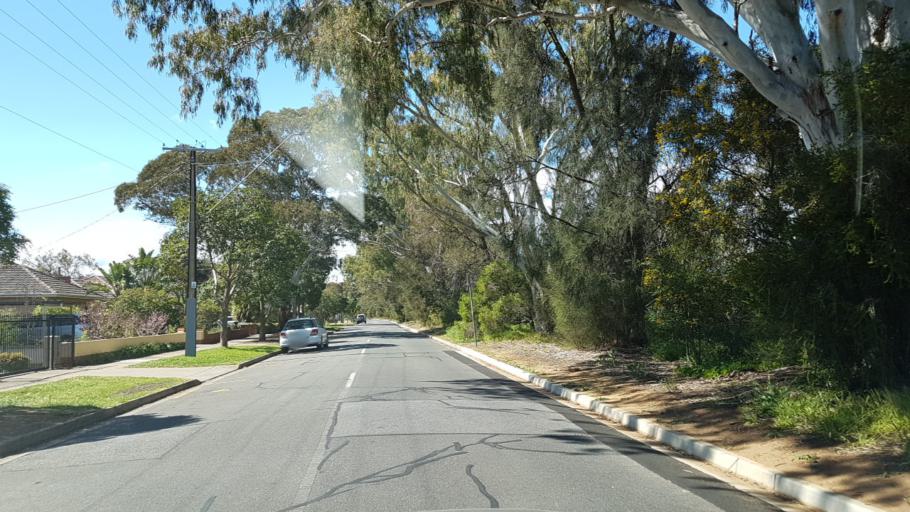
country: AU
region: South Australia
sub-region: Marion
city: Clovelly Park
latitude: -34.9977
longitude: 138.5541
